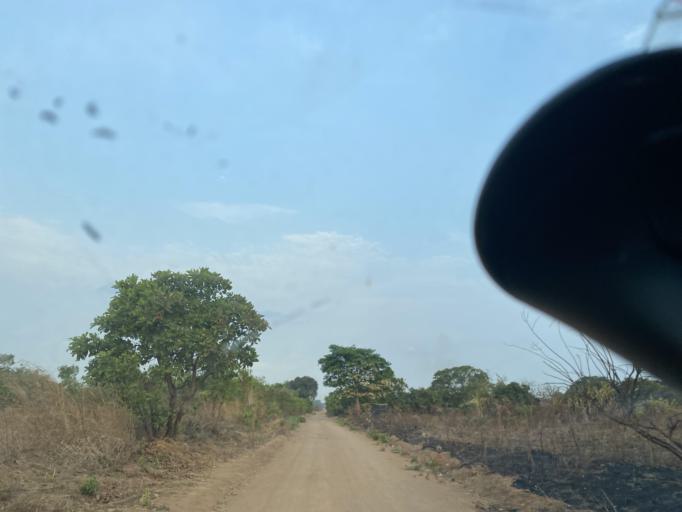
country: ZM
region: Lusaka
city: Chongwe
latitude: -15.2024
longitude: 28.5250
